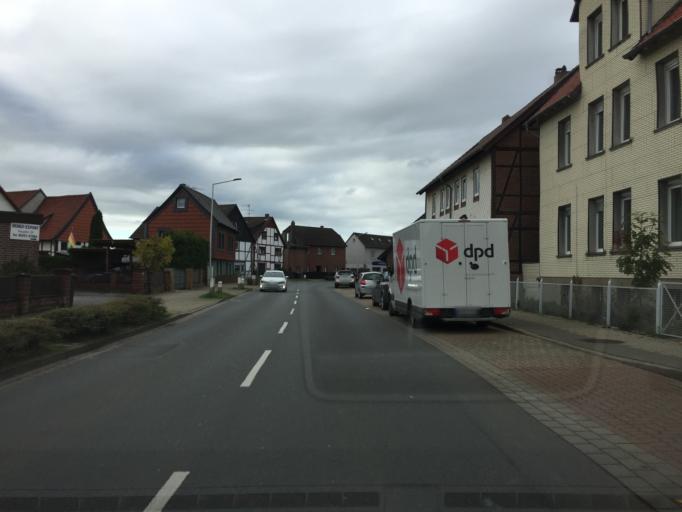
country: DE
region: Lower Saxony
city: Wolfenbuettel
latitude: 52.1716
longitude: 10.5175
